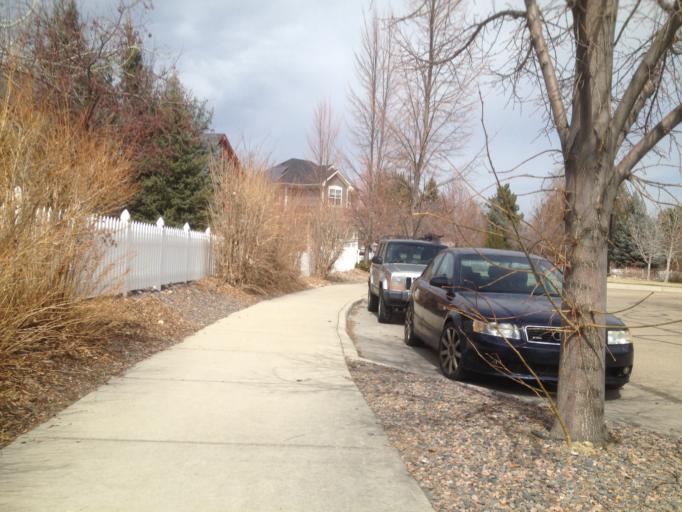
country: US
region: Colorado
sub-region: Boulder County
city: Louisville
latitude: 40.0065
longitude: -105.1400
